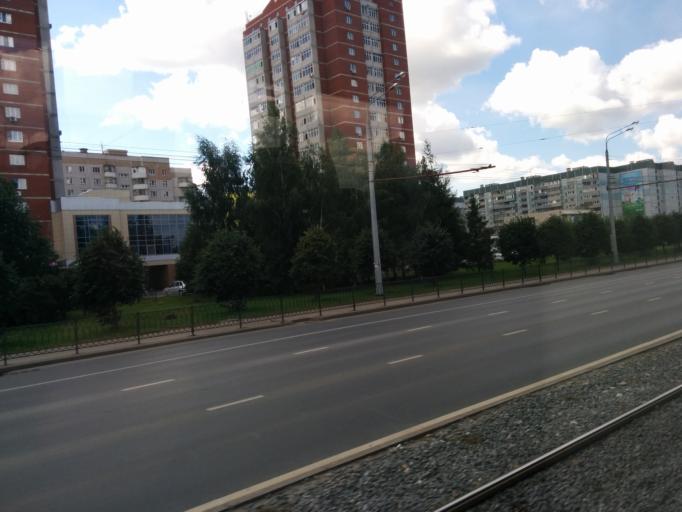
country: RU
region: Tatarstan
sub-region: Gorod Kazan'
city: Kazan
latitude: 55.8271
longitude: 49.1192
